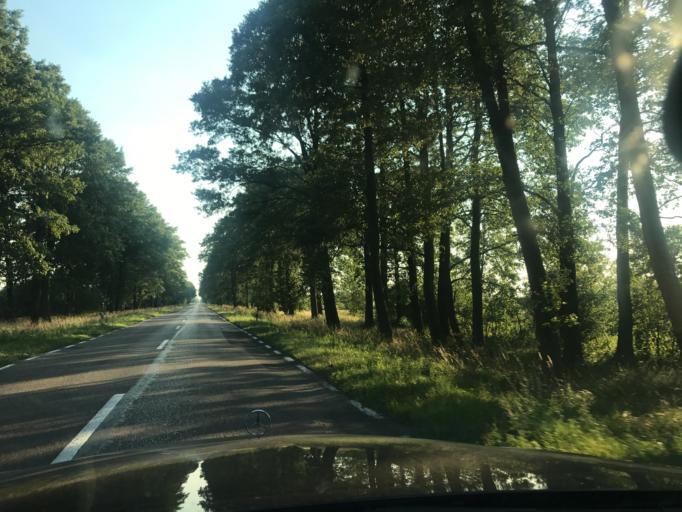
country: PL
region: Lublin Voivodeship
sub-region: Powiat parczewski
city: Jablon
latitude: 51.7419
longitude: 23.1452
